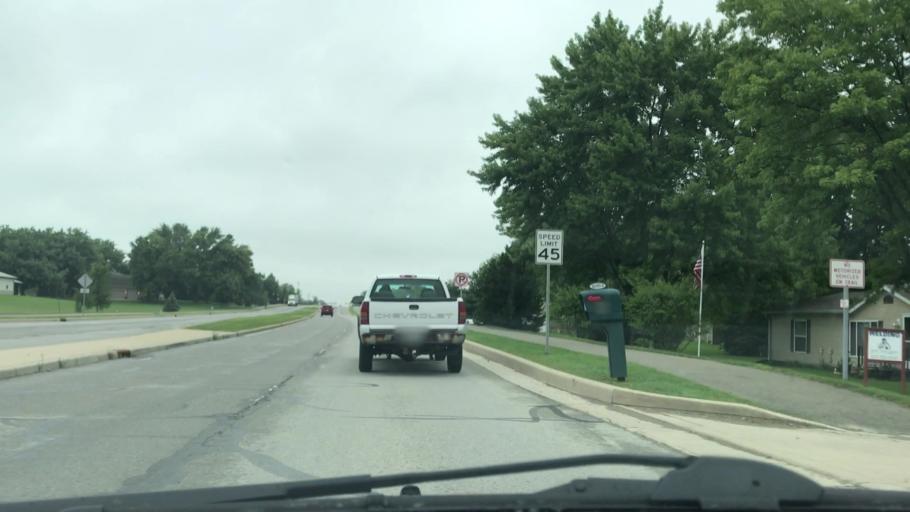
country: US
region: Indiana
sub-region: Hamilton County
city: Westfield
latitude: 40.0336
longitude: -86.0705
